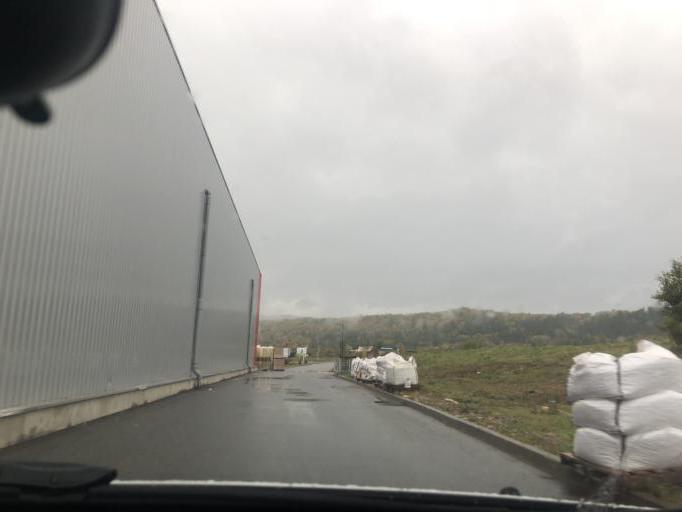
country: FR
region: Provence-Alpes-Cote d'Azur
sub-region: Departement des Alpes-de-Haute-Provence
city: Sisteron
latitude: 44.2361
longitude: 5.9068
